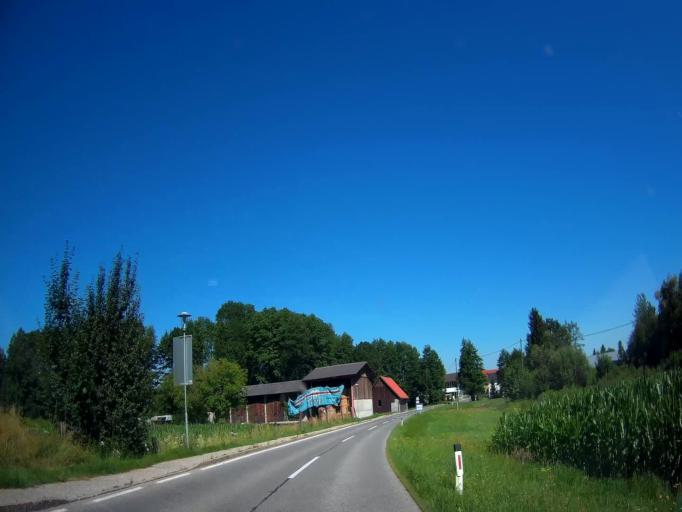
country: AT
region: Carinthia
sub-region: Politischer Bezirk Klagenfurt Land
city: Ebenthal
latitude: 46.6065
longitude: 14.3999
